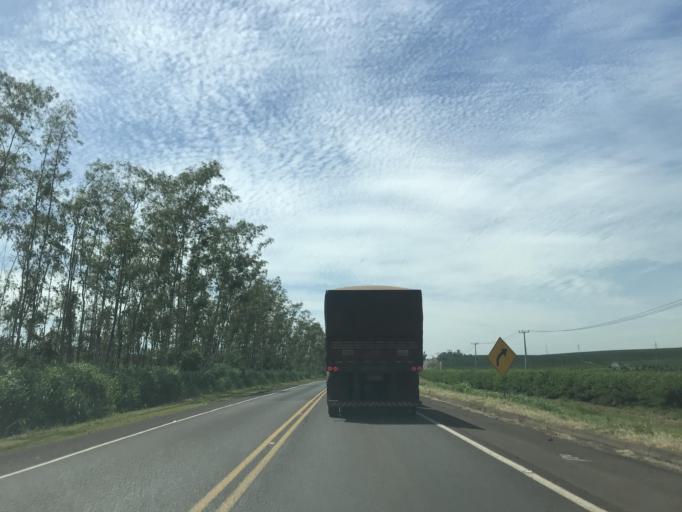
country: BR
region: Parana
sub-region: Paranavai
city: Nova Aurora
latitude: -22.9572
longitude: -52.6571
